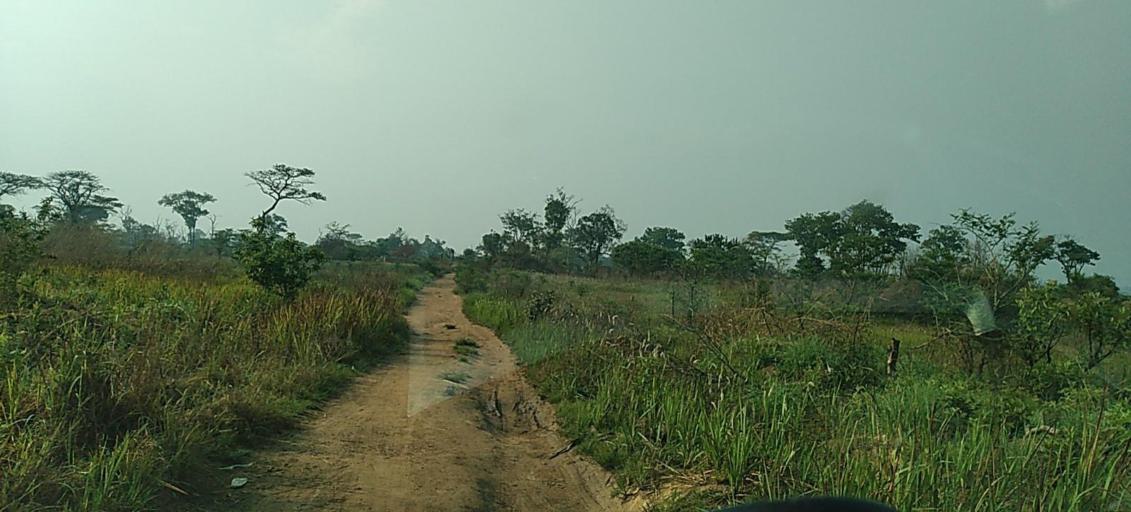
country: ZM
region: North-Western
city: Solwezi
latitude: -12.3614
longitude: 26.5535
